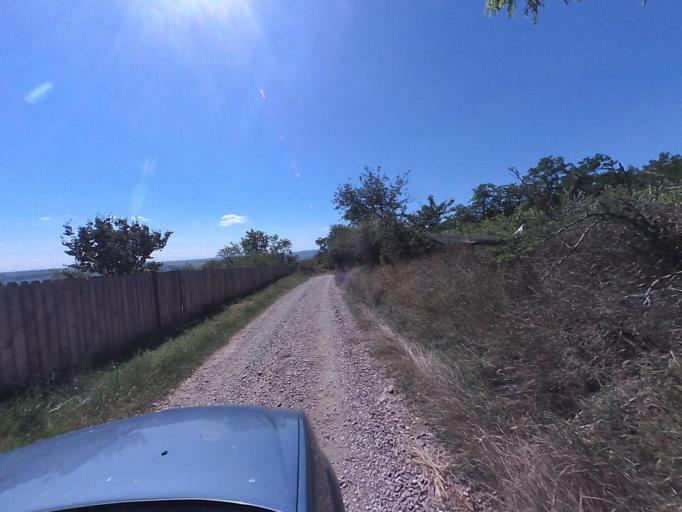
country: RO
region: Vaslui
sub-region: Comuna Costesti
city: Costesti
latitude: 46.4775
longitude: 27.7945
